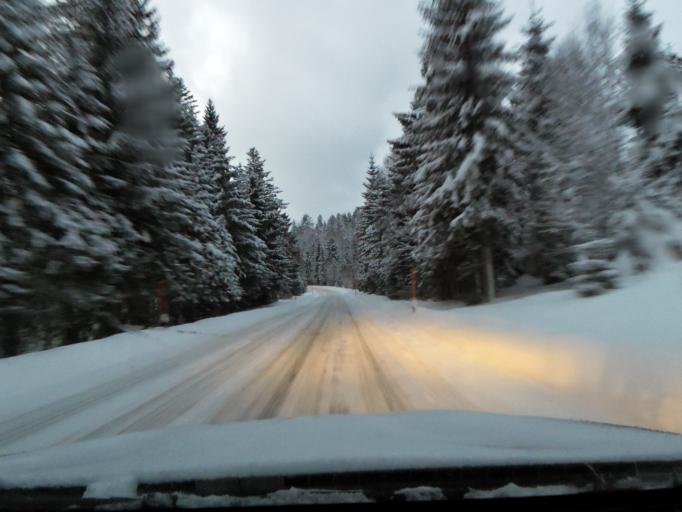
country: DE
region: Bavaria
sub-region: Lower Bavaria
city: Spiegelau
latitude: 48.9199
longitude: 13.3975
